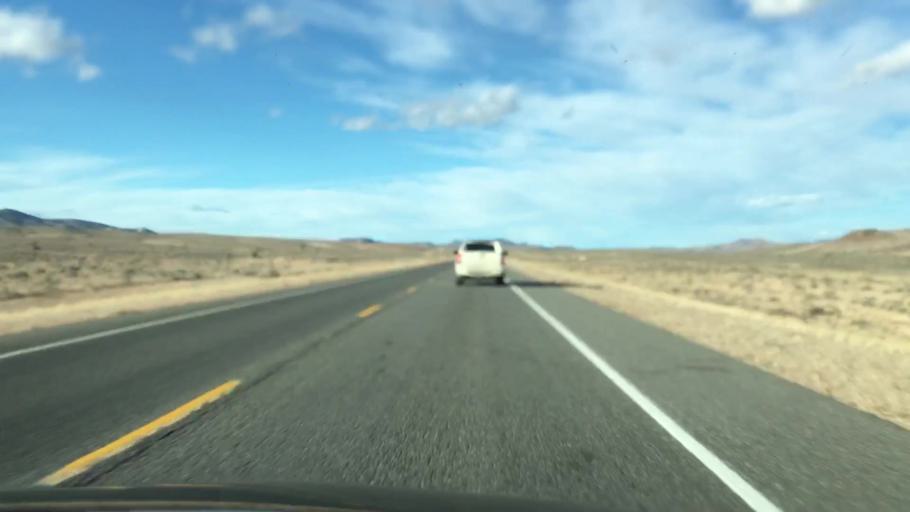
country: US
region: Nevada
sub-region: Esmeralda County
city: Goldfield
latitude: 37.5517
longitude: -117.1977
